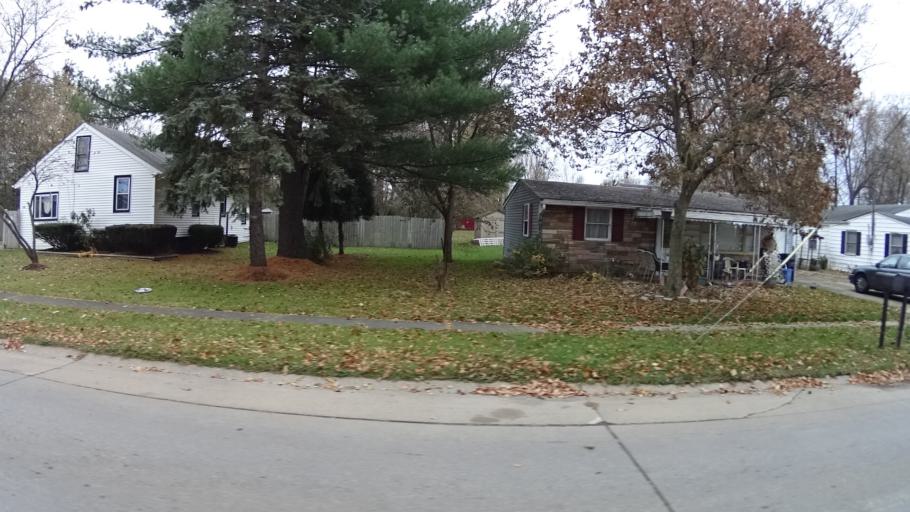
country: US
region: Ohio
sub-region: Lorain County
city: Elyria
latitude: 41.3528
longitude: -82.1184
